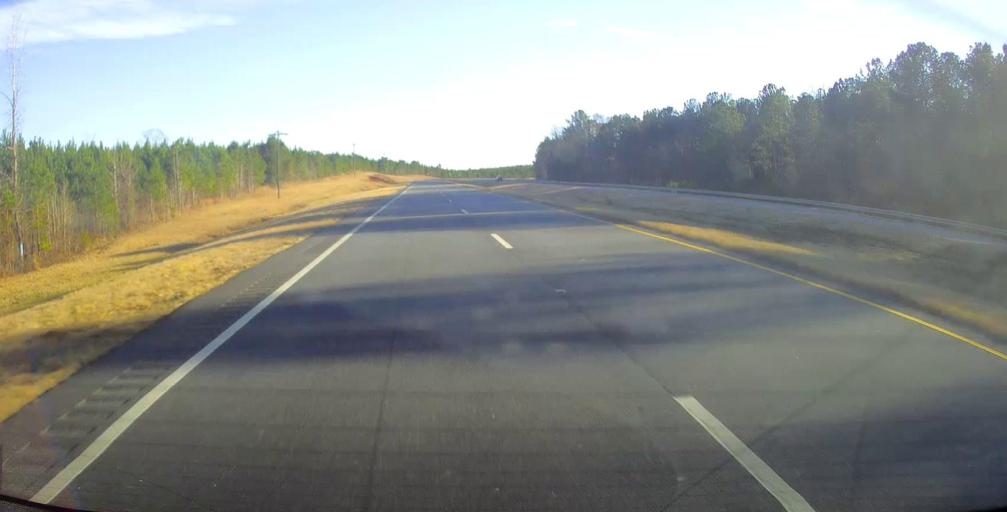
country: US
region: Georgia
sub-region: Upson County
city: Thomaston
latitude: 32.7826
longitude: -84.2459
